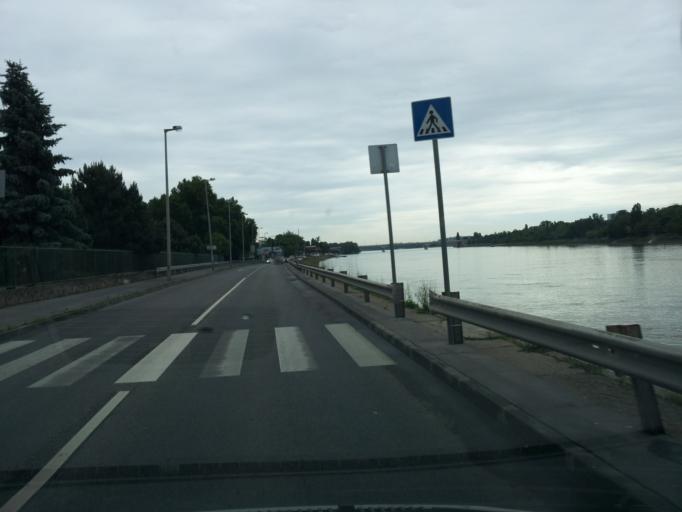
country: HU
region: Budapest
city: Budapest III. keruelet
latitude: 47.5275
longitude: 19.0410
